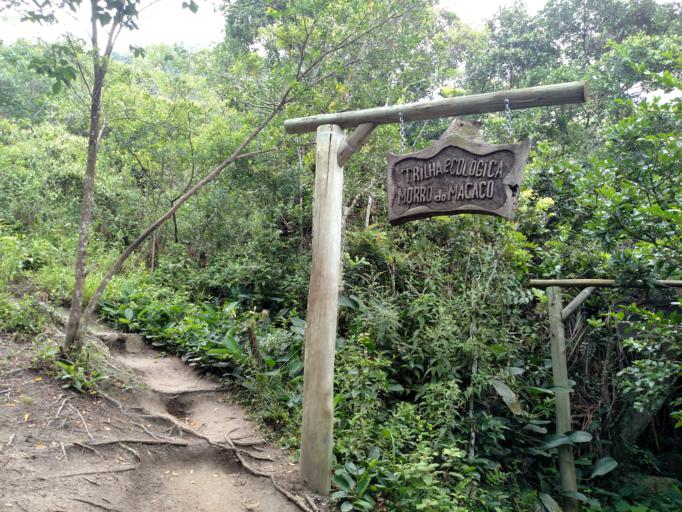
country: BR
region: Santa Catarina
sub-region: Porto Belo
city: Porto Belo
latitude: -27.2014
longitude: -48.4986
